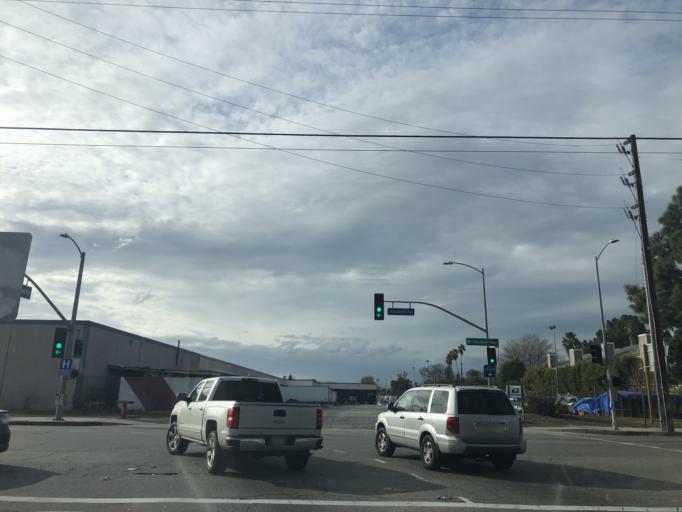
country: US
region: California
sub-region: Los Angeles County
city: Van Nuys
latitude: 34.2028
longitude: -118.4746
